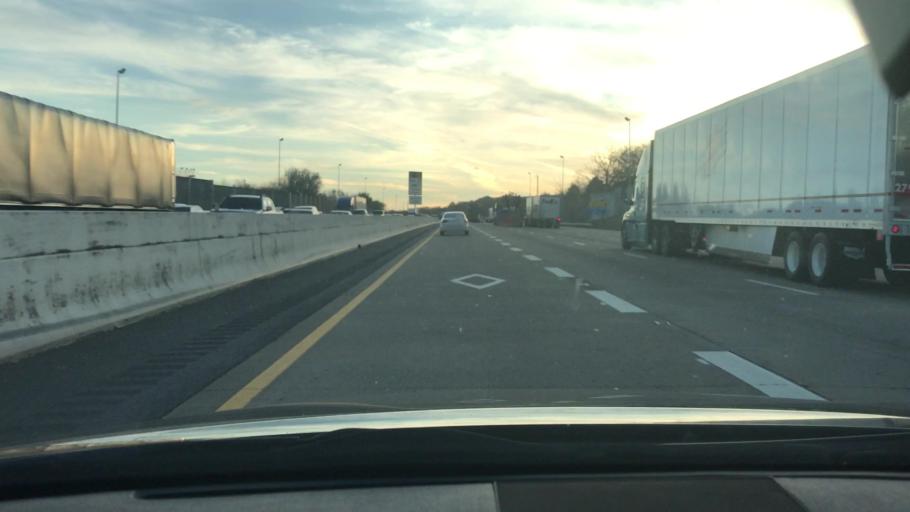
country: US
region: Tennessee
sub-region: Davidson County
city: Goodlettsville
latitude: 36.2862
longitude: -86.7276
